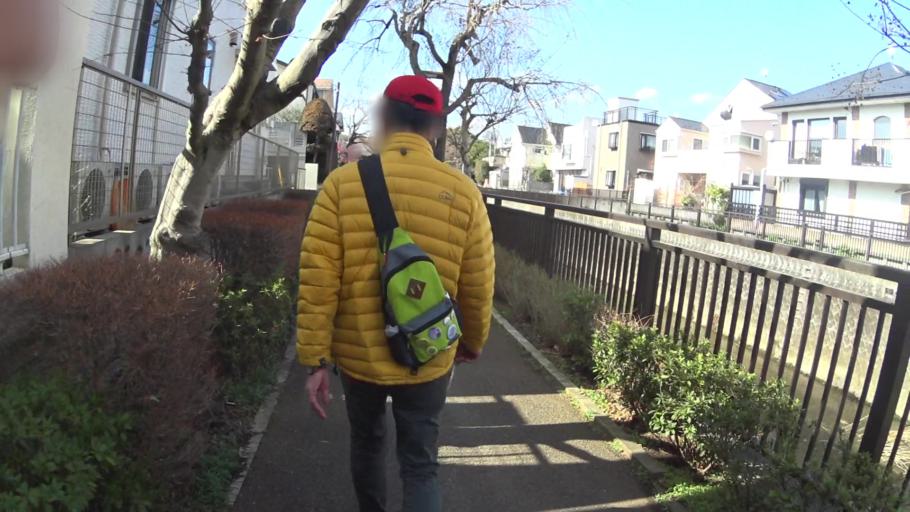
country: JP
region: Tokyo
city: Mitaka-shi
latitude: 35.6519
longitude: 139.6012
